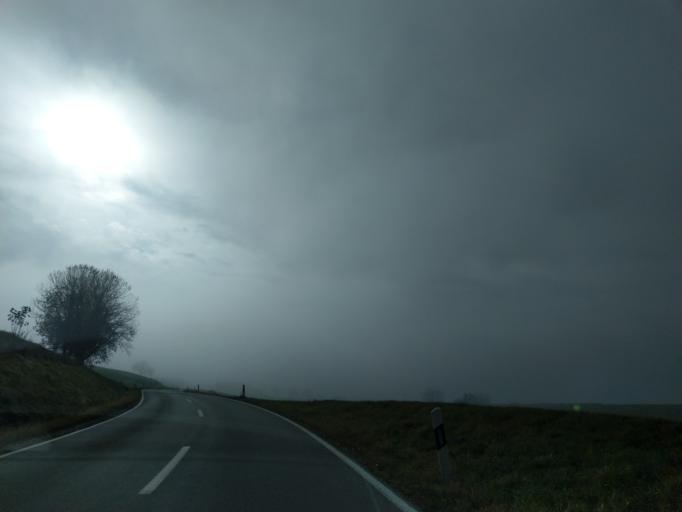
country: DE
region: Bavaria
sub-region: Lower Bavaria
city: Grattersdorf
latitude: 48.7989
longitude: 13.1529
